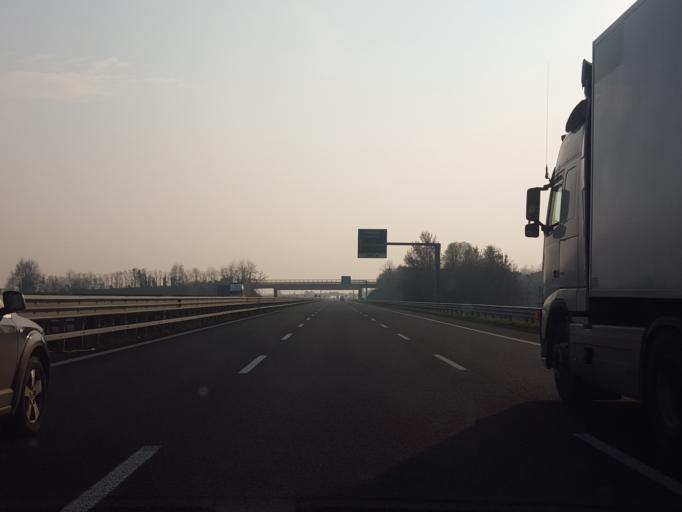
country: IT
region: Veneto
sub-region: Provincia di Treviso
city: Conscio
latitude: 45.5976
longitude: 12.2964
